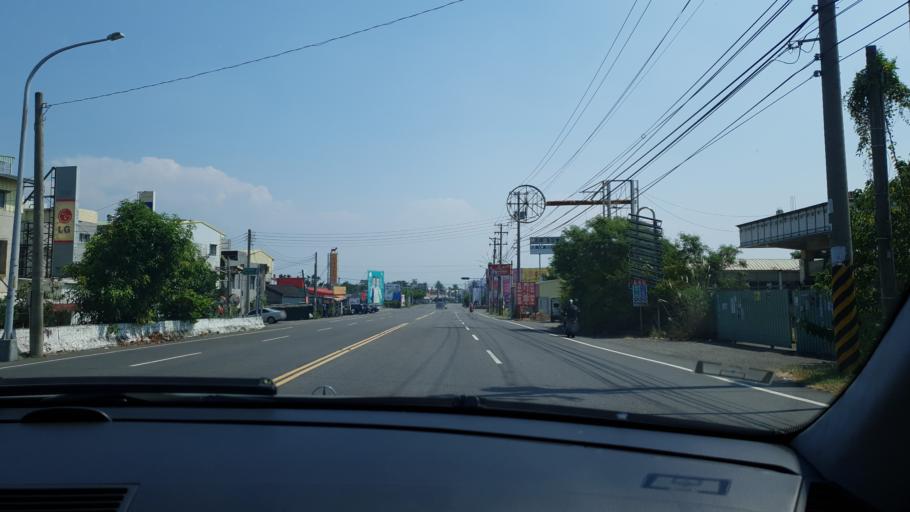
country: TW
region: Taiwan
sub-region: Yunlin
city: Douliu
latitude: 23.7291
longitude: 120.5214
